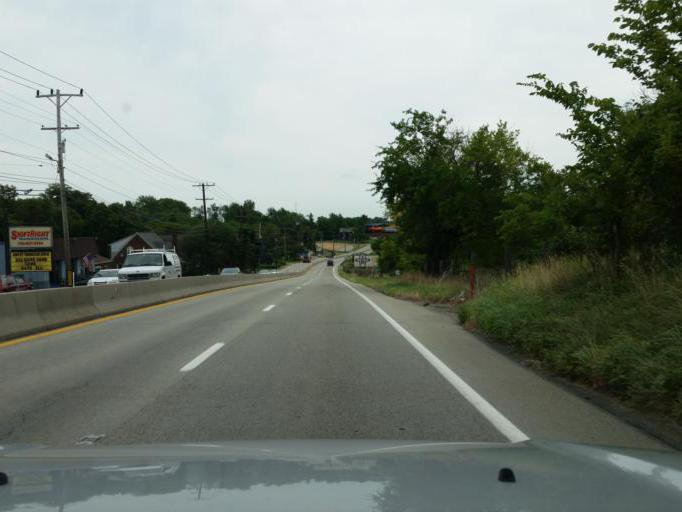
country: US
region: Pennsylvania
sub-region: Westmoreland County
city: Manor
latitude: 40.3091
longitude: -79.6472
